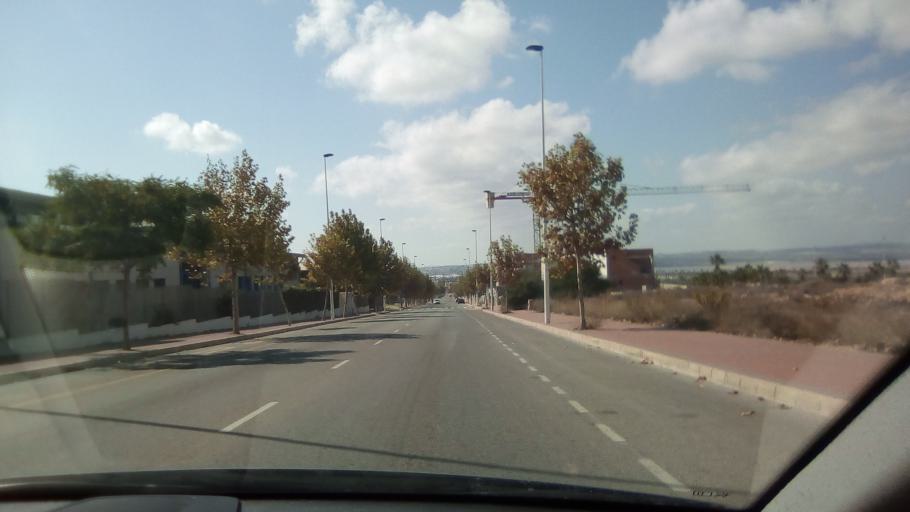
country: ES
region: Valencia
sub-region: Provincia de Alicante
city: Torrevieja
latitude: 38.0044
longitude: -0.6715
